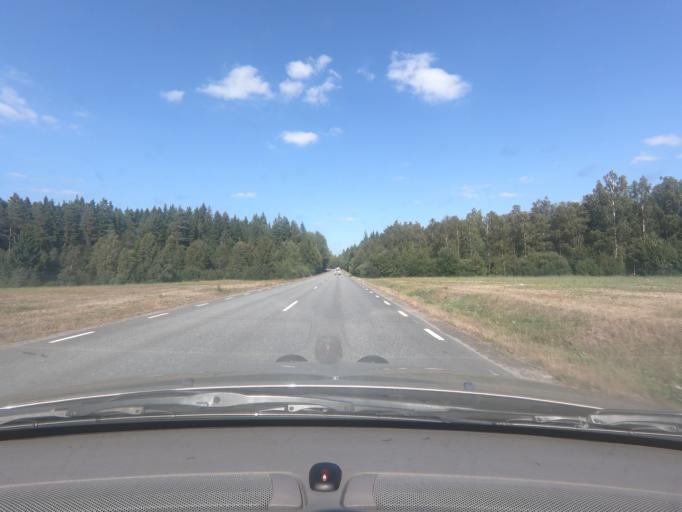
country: SE
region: Joenkoeping
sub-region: Vetlanda Kommun
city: Landsbro
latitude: 57.3907
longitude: 14.9796
